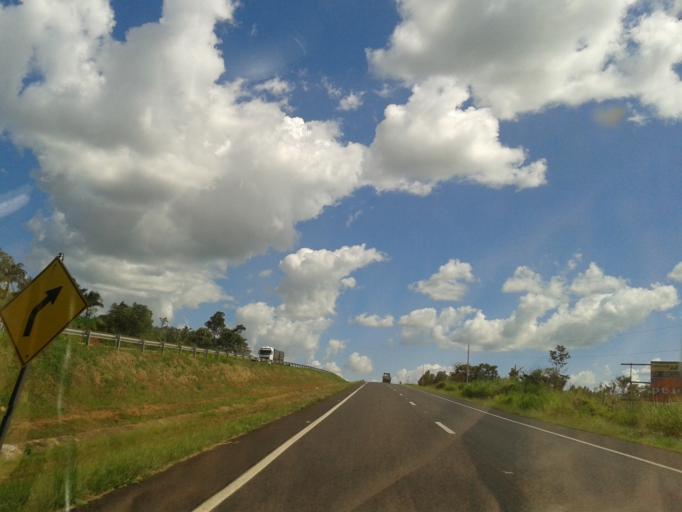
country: BR
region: Goias
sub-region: Morrinhos
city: Morrinhos
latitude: -17.6930
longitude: -49.1566
